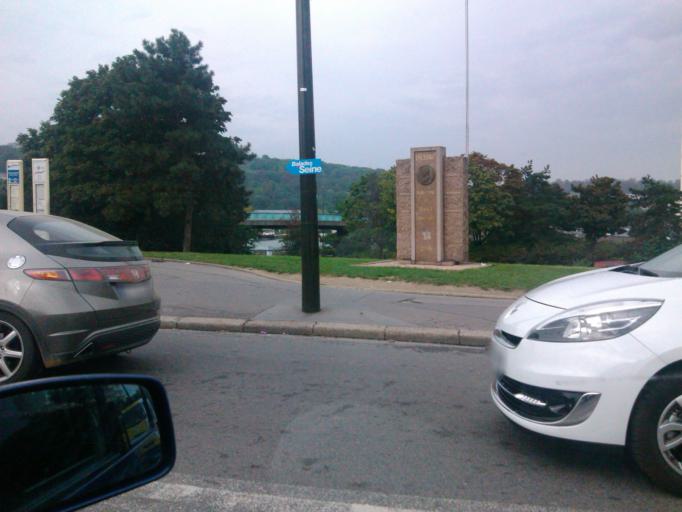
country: FR
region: Ile-de-France
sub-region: Departement des Hauts-de-Seine
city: Sevres
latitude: 48.8296
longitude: 2.2294
